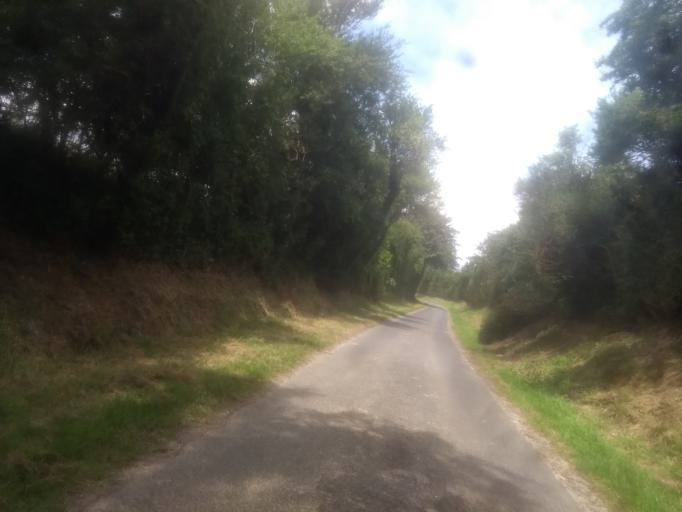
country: FR
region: Nord-Pas-de-Calais
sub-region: Departement du Pas-de-Calais
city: Beaumetz-les-Loges
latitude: 50.2282
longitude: 2.6391
